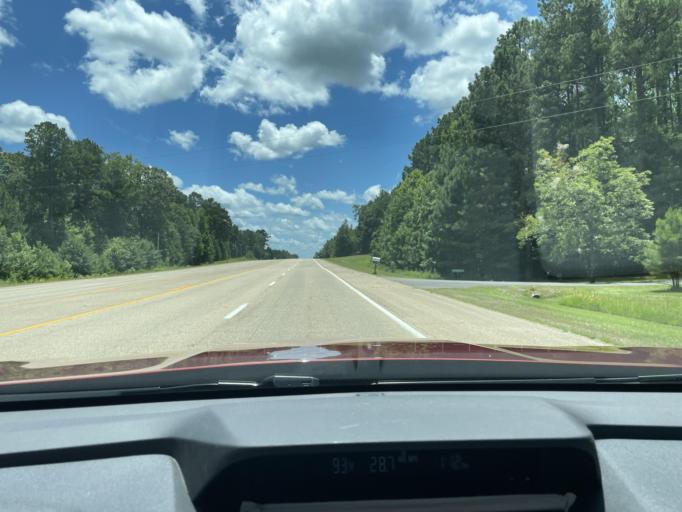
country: US
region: Arkansas
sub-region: Drew County
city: Monticello
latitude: 33.6893
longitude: -91.8061
